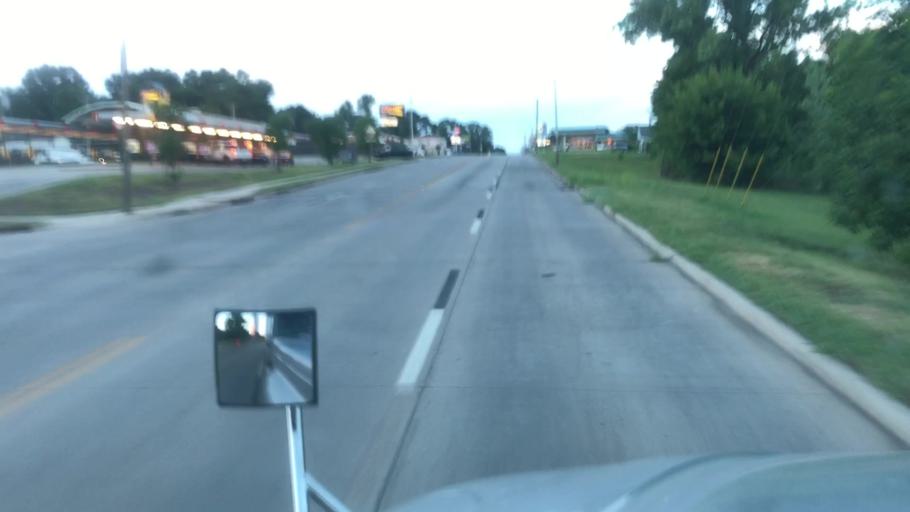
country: US
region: Oklahoma
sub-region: Kay County
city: Ponca City
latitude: 36.6970
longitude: -97.0672
